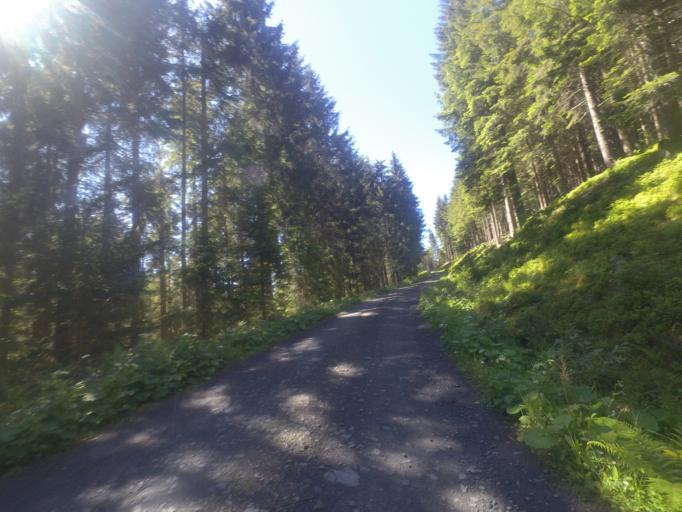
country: AT
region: Salzburg
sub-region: Politischer Bezirk Zell am See
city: Lend
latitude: 47.3252
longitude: 13.0519
